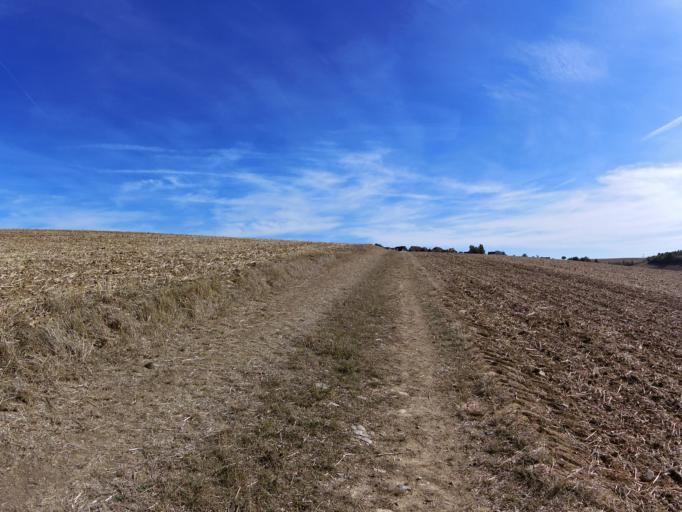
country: DE
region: Bavaria
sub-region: Regierungsbezirk Unterfranken
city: Eisingen
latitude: 49.7675
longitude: 9.8219
